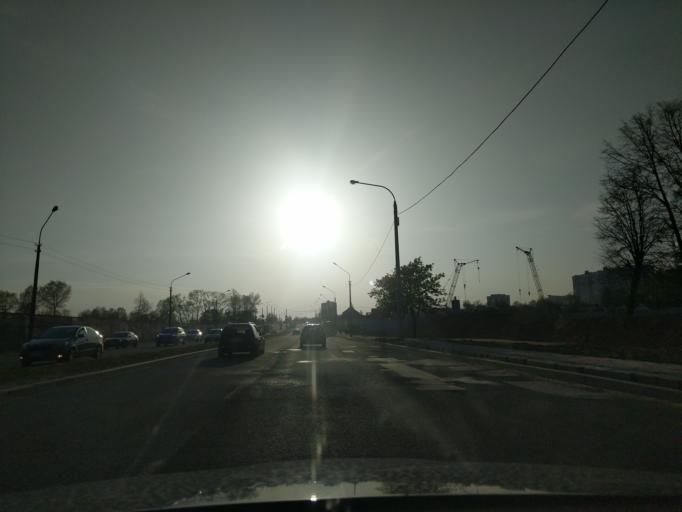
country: BY
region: Minsk
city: Minsk
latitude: 53.8722
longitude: 27.5515
